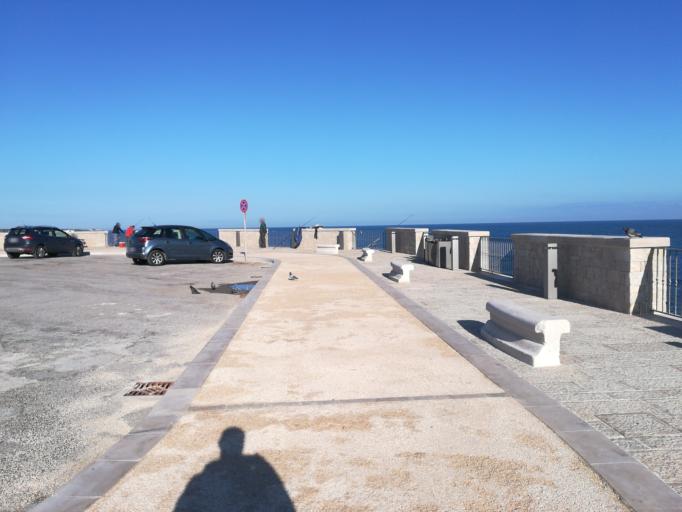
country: IT
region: Apulia
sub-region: Provincia di Bari
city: Polignano a Mare
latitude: 40.9967
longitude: 17.2241
